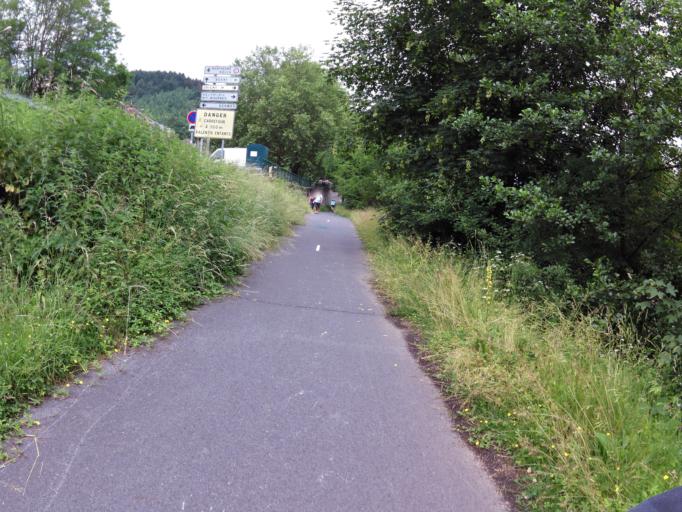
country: FR
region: Champagne-Ardenne
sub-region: Departement des Ardennes
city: Nouzonville
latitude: 49.8152
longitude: 4.7402
